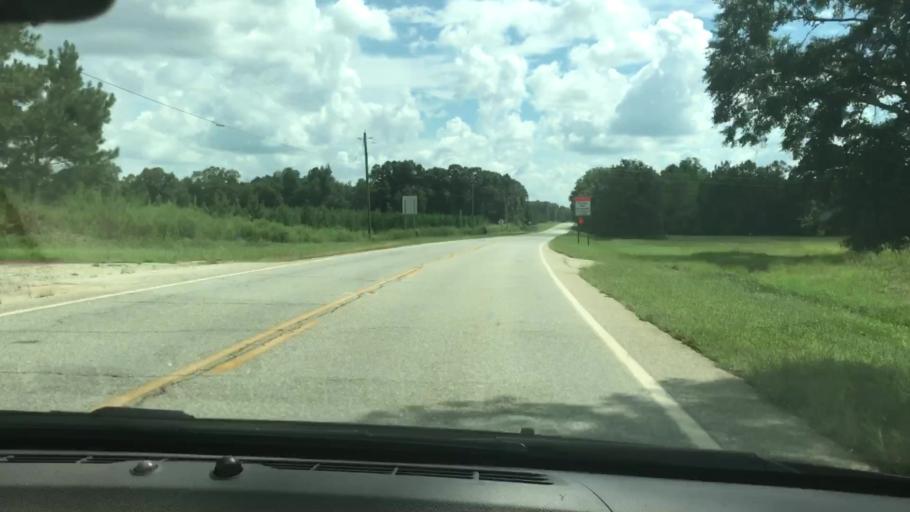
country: US
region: Georgia
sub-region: Clay County
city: Fort Gaines
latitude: 31.7122
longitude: -85.0415
